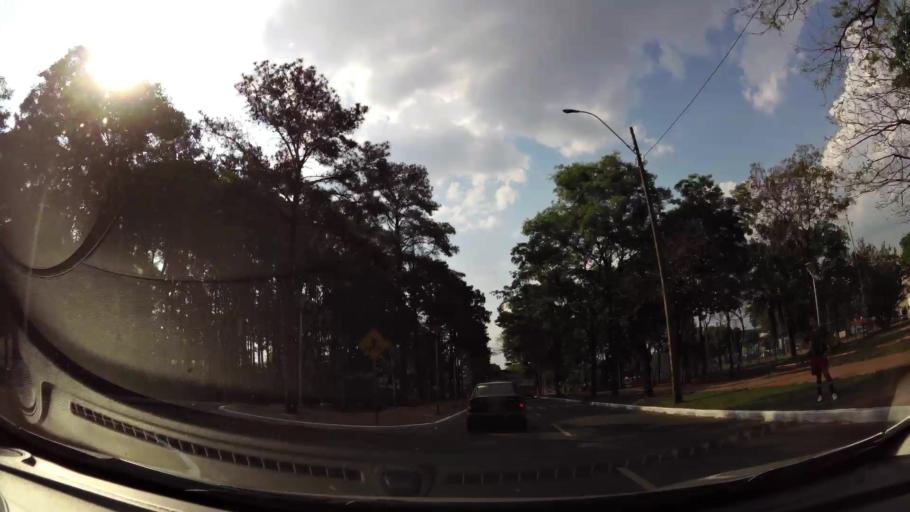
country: PY
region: Alto Parana
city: Ciudad del Este
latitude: -25.5217
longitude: -54.6126
